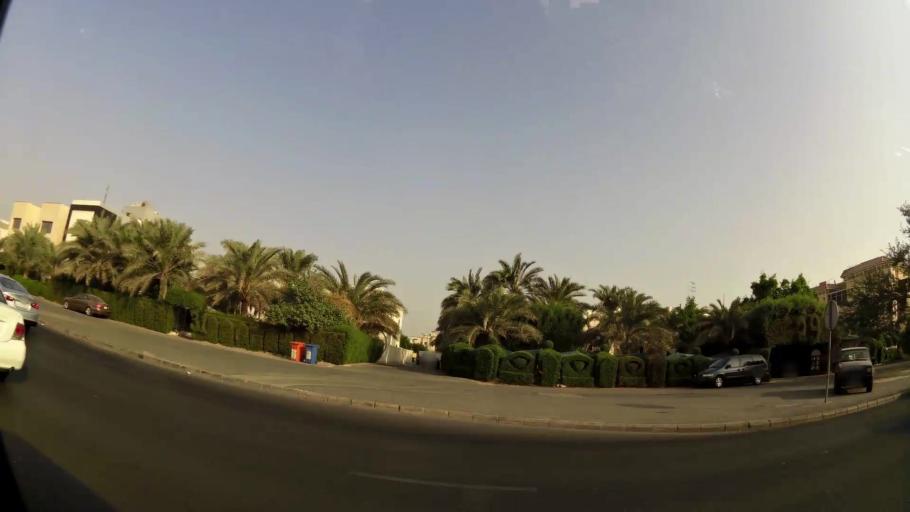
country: KW
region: Muhafazat Hawalli
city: Hawalli
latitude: 29.3214
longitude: 48.0002
